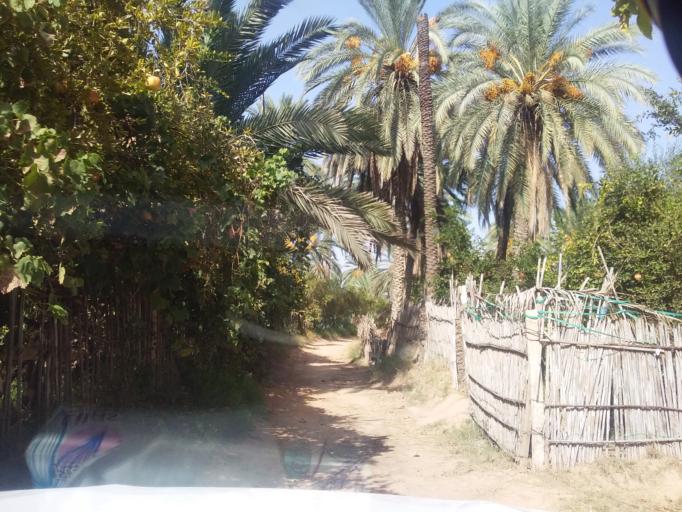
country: TN
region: Qabis
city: Gabes
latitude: 33.6257
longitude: 10.2902
